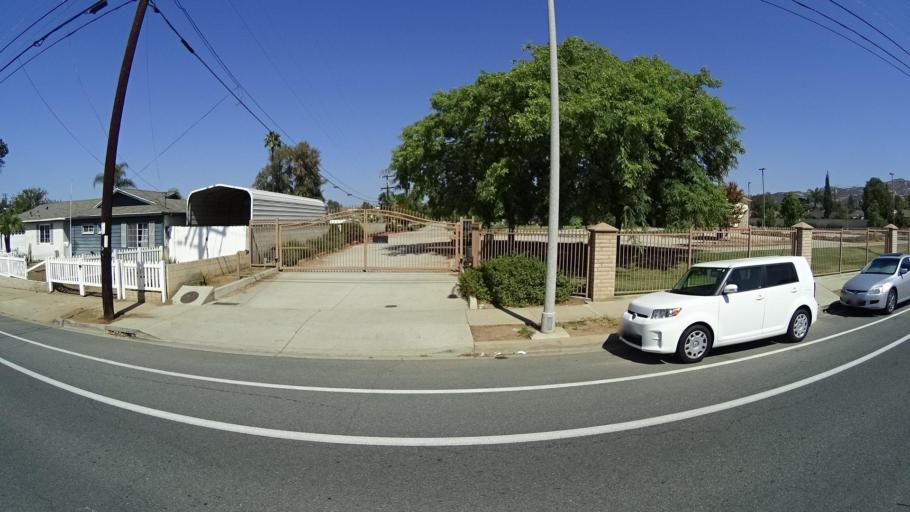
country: US
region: California
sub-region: San Diego County
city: Bostonia
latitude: 32.8003
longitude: -116.9214
